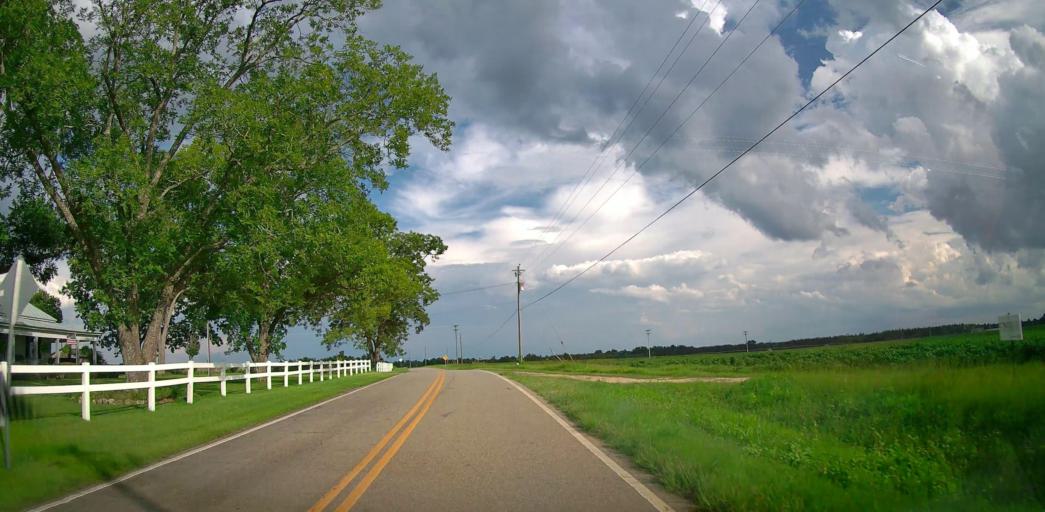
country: US
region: Georgia
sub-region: Bleckley County
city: Cochran
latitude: 32.4000
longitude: -83.3751
